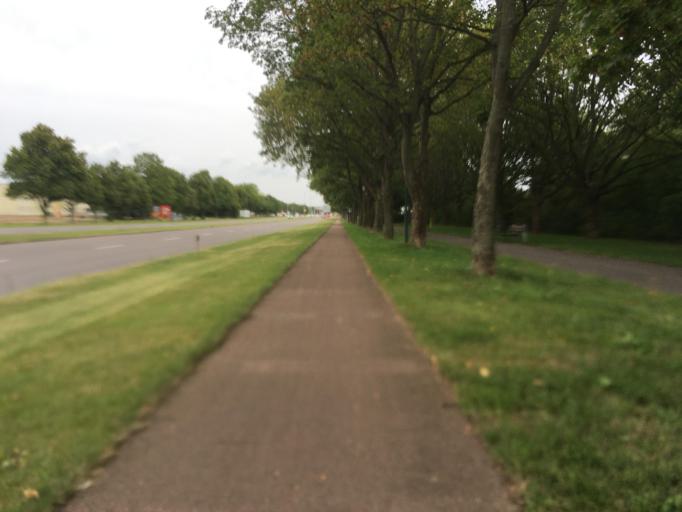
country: DE
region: Brandenburg
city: Schwedt (Oder)
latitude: 53.0665
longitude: 14.2638
